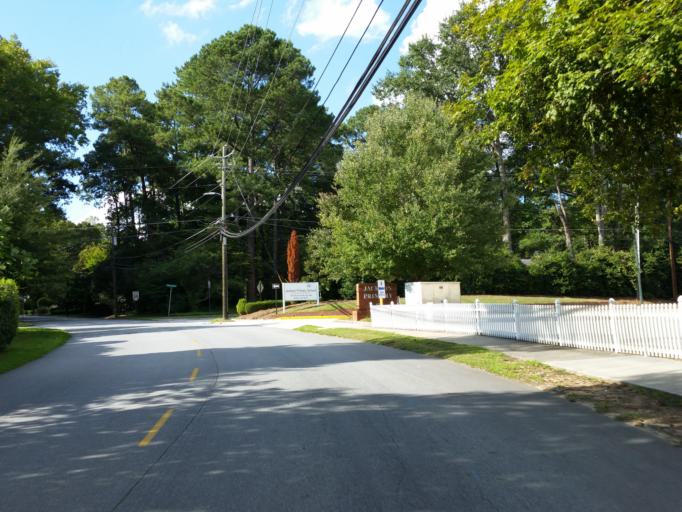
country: US
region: Georgia
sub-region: Cobb County
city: Vinings
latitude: 33.8696
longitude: -84.4071
